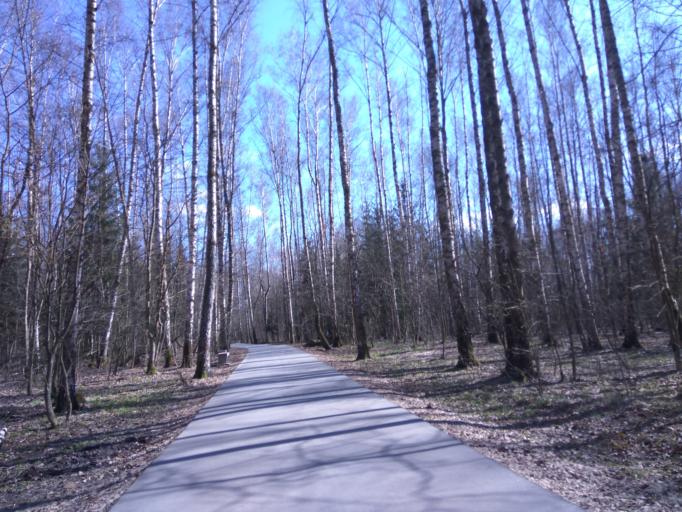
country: RU
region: Moscow
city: Ivanovskoye
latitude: 55.7885
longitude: 37.8266
